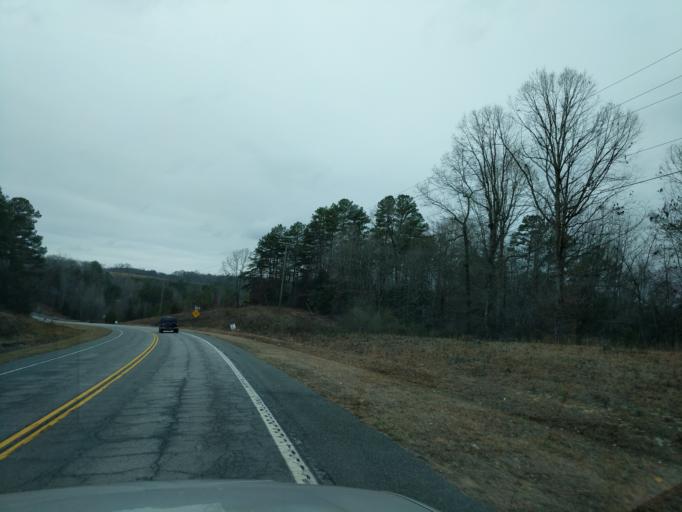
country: US
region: South Carolina
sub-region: Oconee County
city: Walhalla
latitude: 34.8434
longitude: -83.0368
